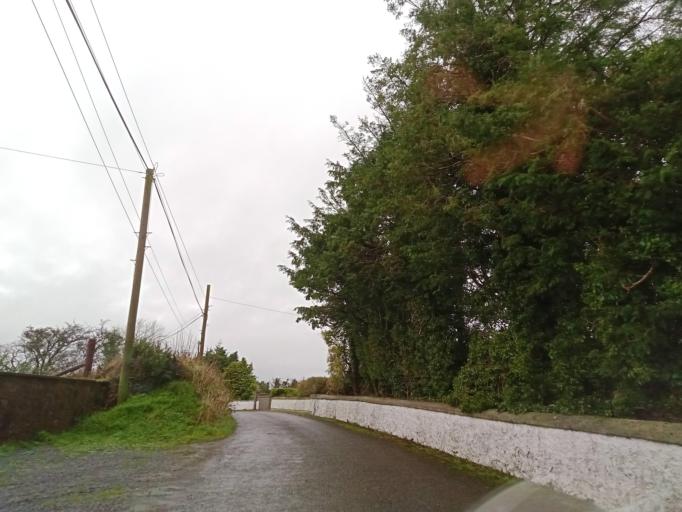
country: IE
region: Munster
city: Fethard
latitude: 52.5563
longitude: -7.7000
